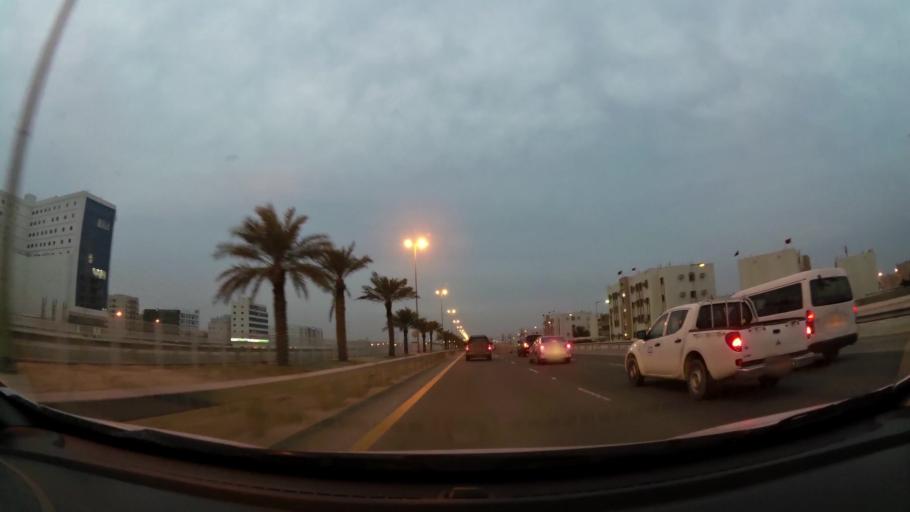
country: BH
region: Northern
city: Ar Rifa'
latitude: 26.1545
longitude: 50.5705
